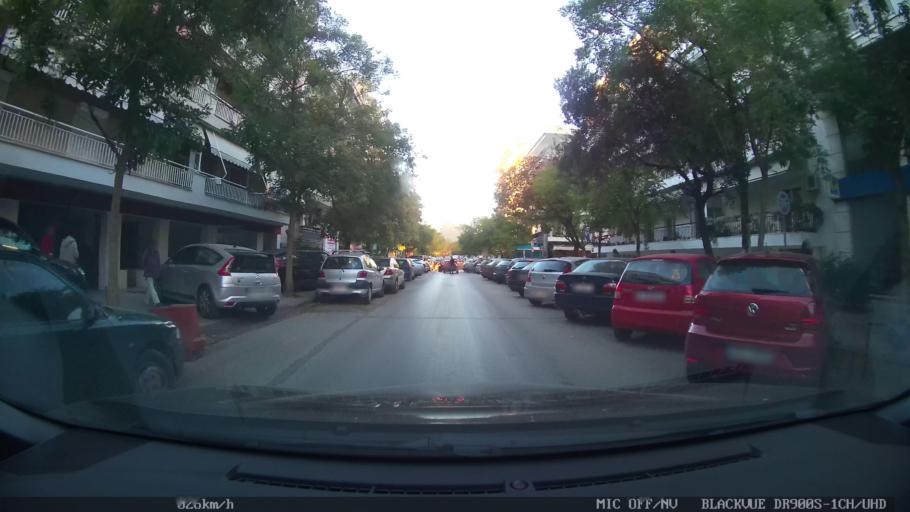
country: GR
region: Central Macedonia
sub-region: Nomos Thessalonikis
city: Triandria
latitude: 40.6085
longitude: 22.9806
